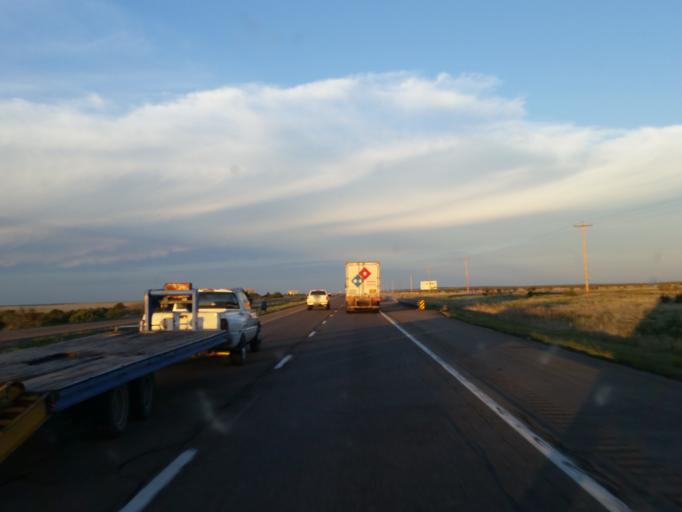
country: US
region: New Mexico
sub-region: San Miguel County
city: Las Vegas
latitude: 34.9933
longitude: -105.3349
